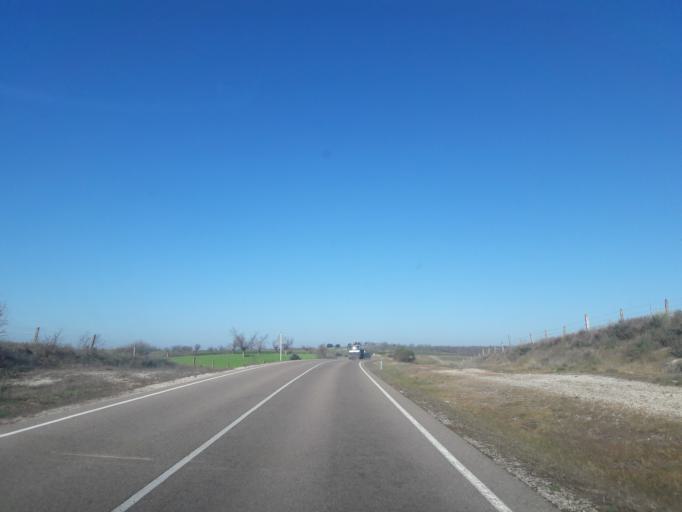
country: ES
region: Castille and Leon
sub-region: Provincia de Salamanca
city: Valderrodrigo
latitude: 41.0735
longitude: -6.5339
